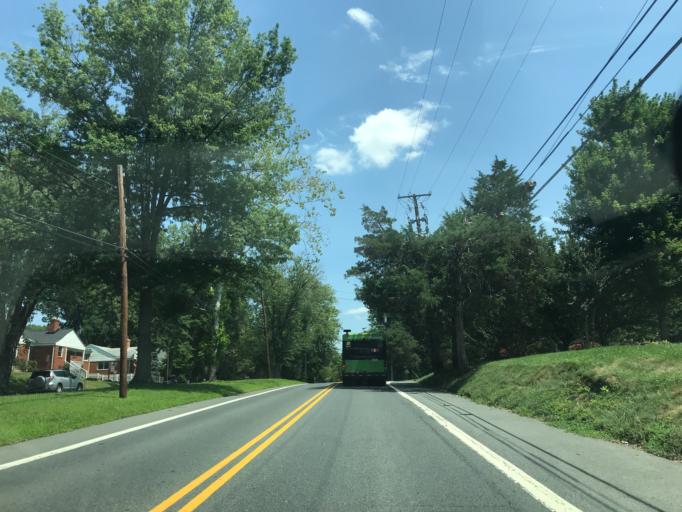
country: US
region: Maryland
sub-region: Montgomery County
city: North Bethesda
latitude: 39.0346
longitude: -77.1001
